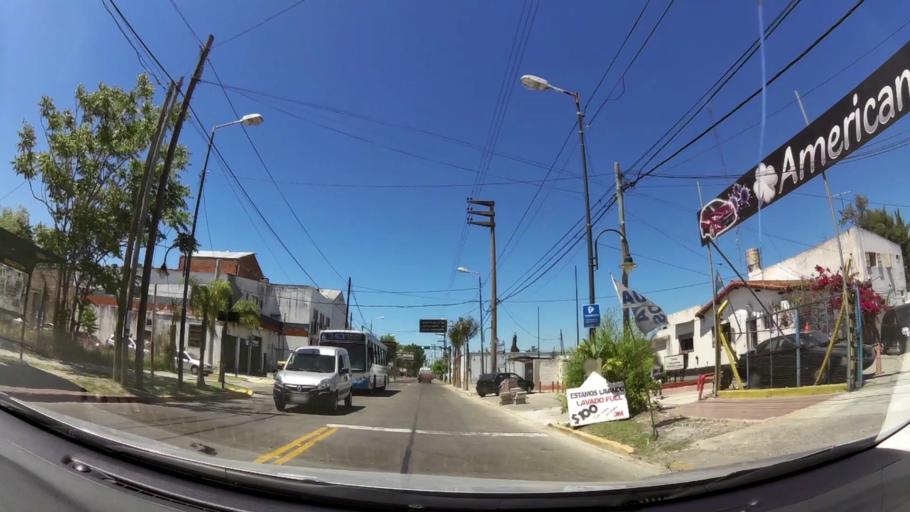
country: AR
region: Buenos Aires
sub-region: Partido de Tigre
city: Tigre
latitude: -34.4549
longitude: -58.5524
